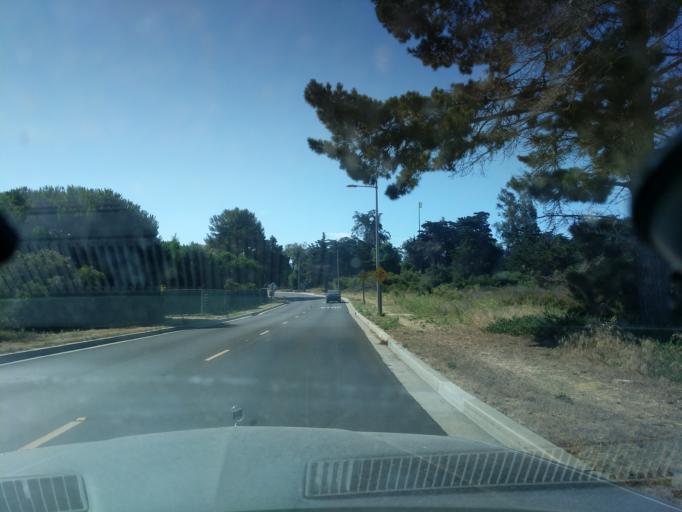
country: US
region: California
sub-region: Santa Barbara County
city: Isla Vista
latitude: 34.4227
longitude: -119.8542
